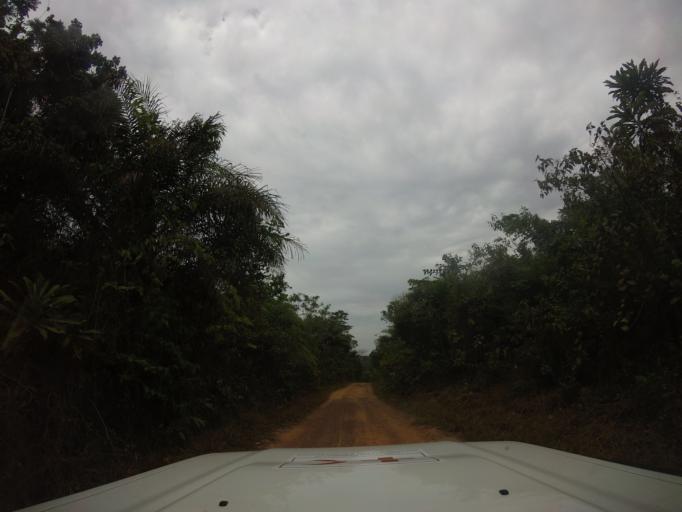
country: SL
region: Southern Province
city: Zimmi
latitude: 7.2044
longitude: -11.2110
